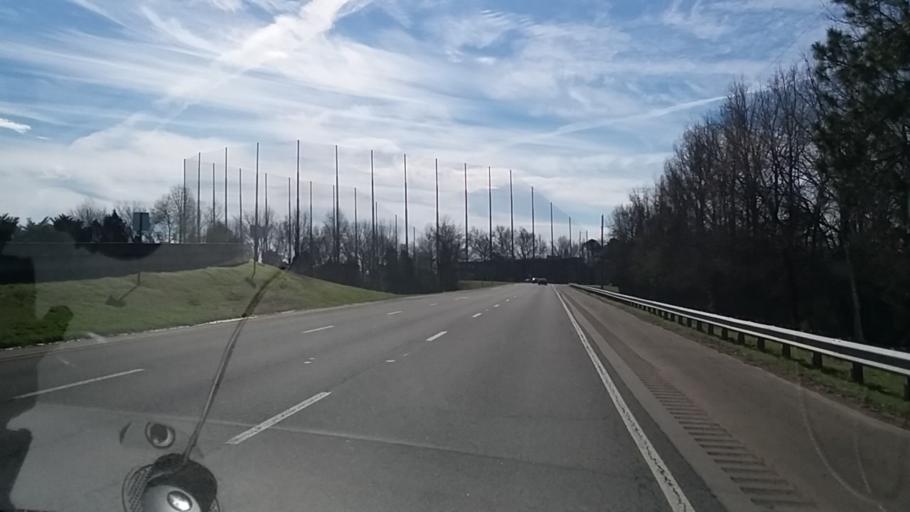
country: US
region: Alabama
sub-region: Madison County
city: Redstone Arsenal
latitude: 34.7413
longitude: -86.6719
